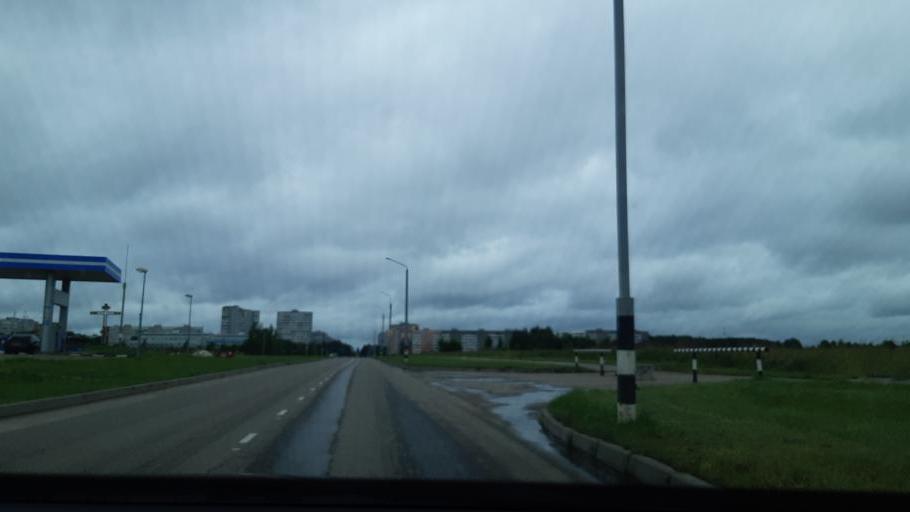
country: RU
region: Smolensk
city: Desnogorsk
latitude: 54.1417
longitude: 33.2790
